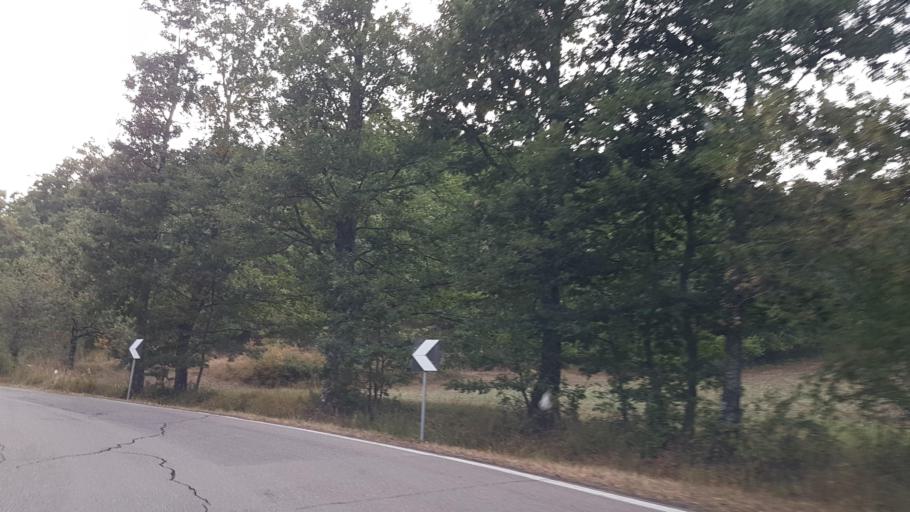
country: IT
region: Emilia-Romagna
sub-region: Provincia di Parma
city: Albareto
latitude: 44.4579
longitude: 9.6700
